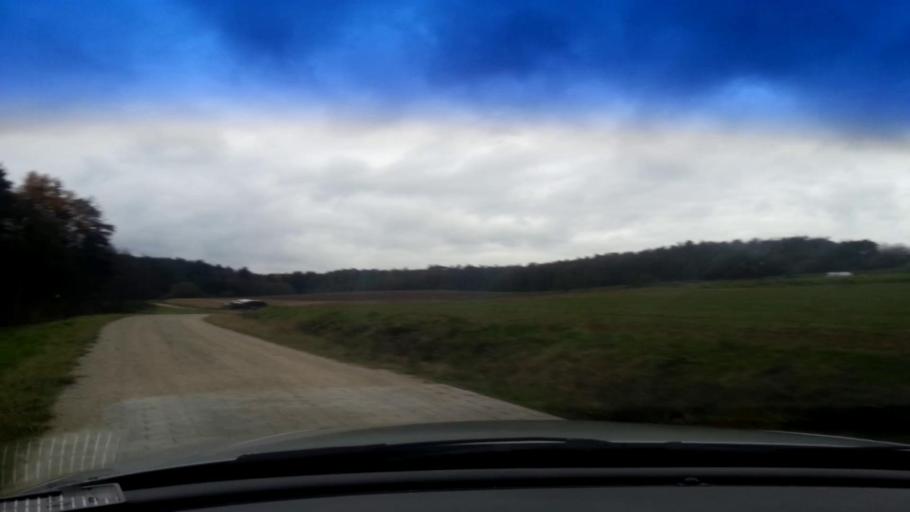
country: DE
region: Bavaria
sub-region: Upper Franconia
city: Walsdorf
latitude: 49.8587
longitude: 10.7976
